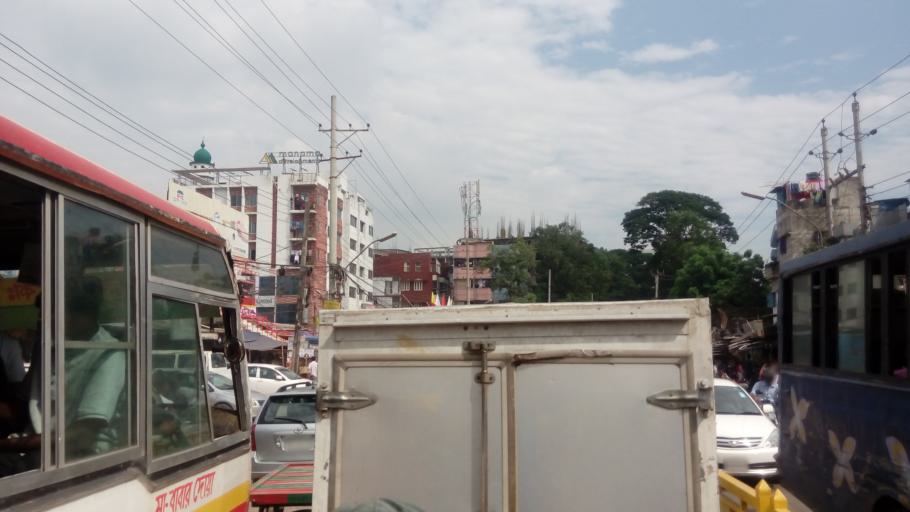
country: BD
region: Dhaka
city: Azimpur
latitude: 23.7598
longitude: 90.3666
